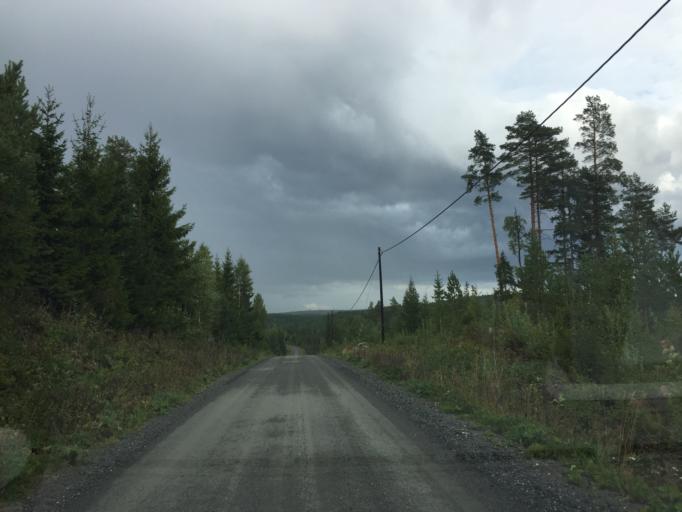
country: SE
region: Vaermland
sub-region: Filipstads Kommun
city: Lesjofors
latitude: 59.9152
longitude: 14.1181
